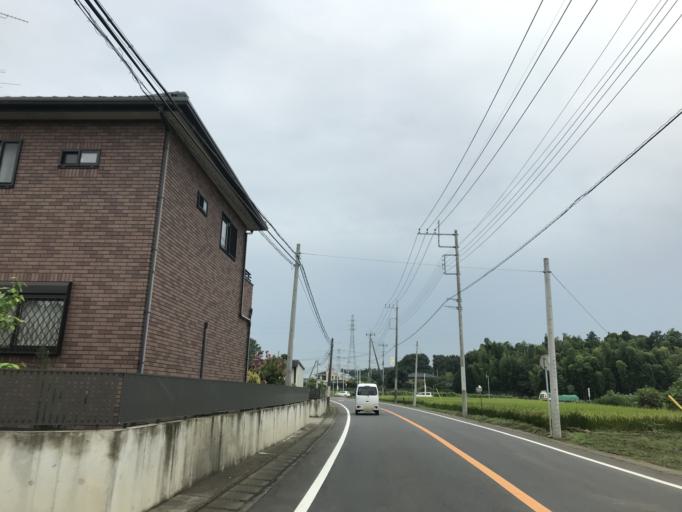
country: JP
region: Ibaraki
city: Sakai
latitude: 36.1006
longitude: 139.8040
